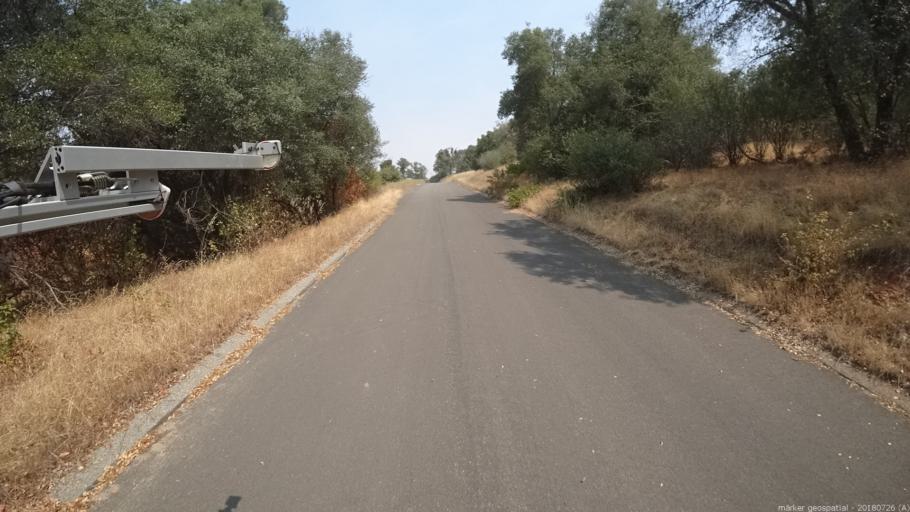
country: US
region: California
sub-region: Madera County
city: Coarsegold
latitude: 37.2526
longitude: -119.6854
